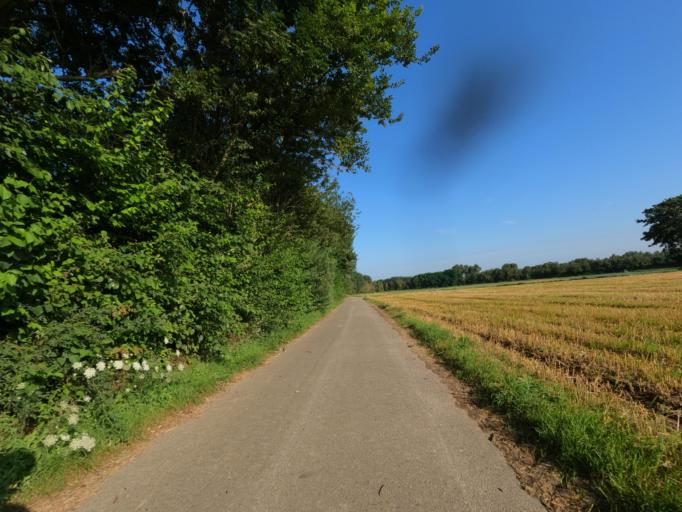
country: DE
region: North Rhine-Westphalia
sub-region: Regierungsbezirk Dusseldorf
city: Grevenbroich
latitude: 51.0982
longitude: 6.5471
